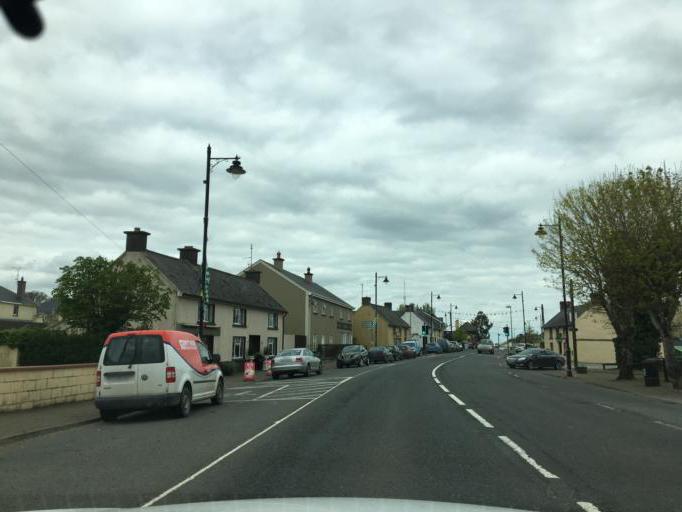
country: IE
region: Leinster
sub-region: Loch Garman
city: Enniscorthy
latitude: 52.4493
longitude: -6.7192
